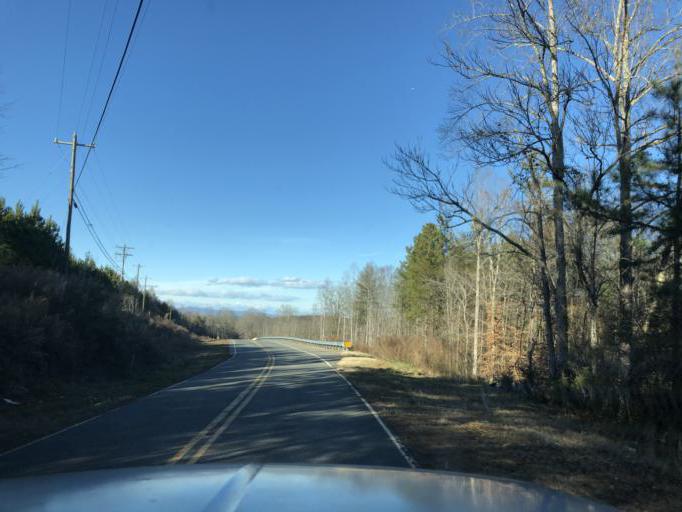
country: US
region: North Carolina
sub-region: Cleveland County
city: Shelby
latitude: 35.3228
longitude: -81.5385
